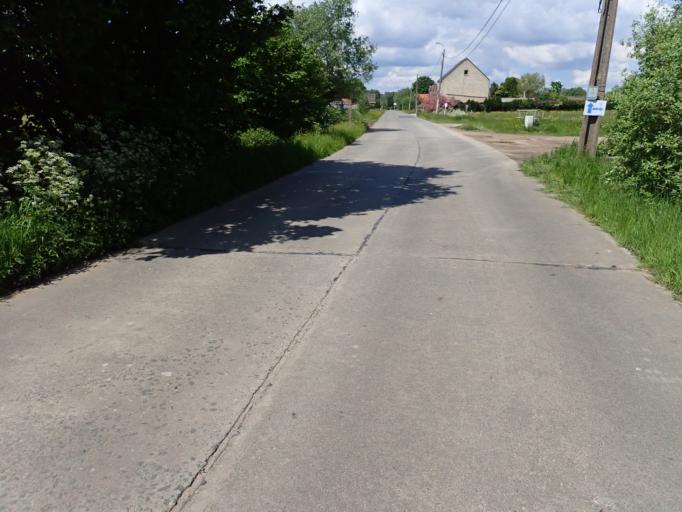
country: BE
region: Flanders
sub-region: Provincie Oost-Vlaanderen
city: Dendermonde
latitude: 51.0056
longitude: 4.0998
